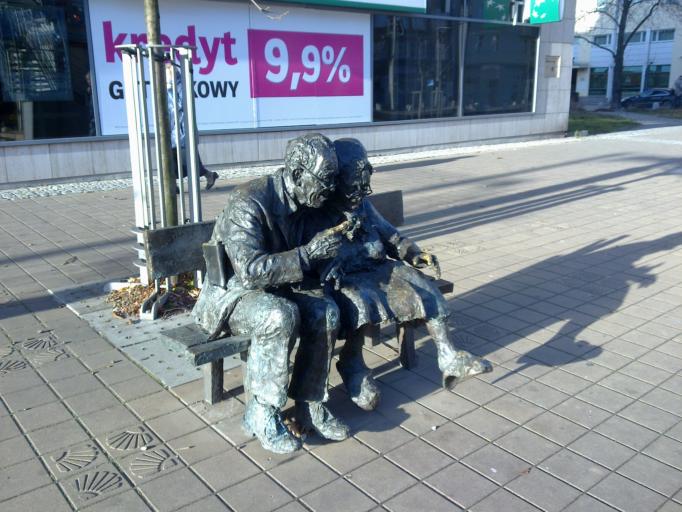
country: PL
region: Pomeranian Voivodeship
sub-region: Gdynia
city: Gdynia
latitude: 54.5230
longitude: 18.5435
